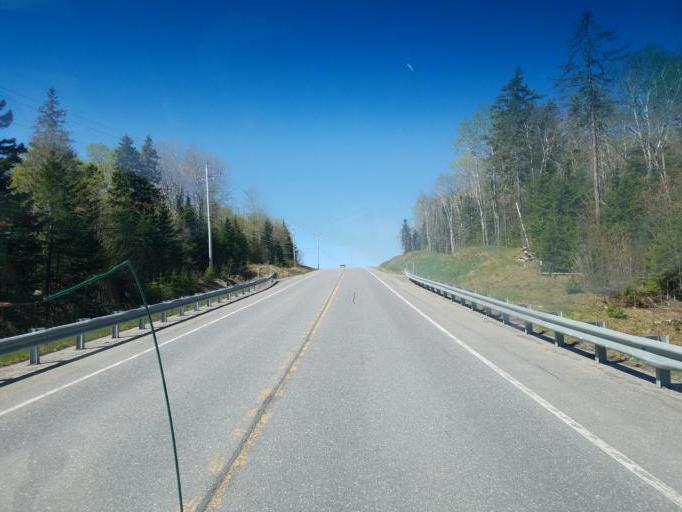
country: US
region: Maine
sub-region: Aroostook County
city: Presque Isle
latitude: 46.6653
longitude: -68.2254
